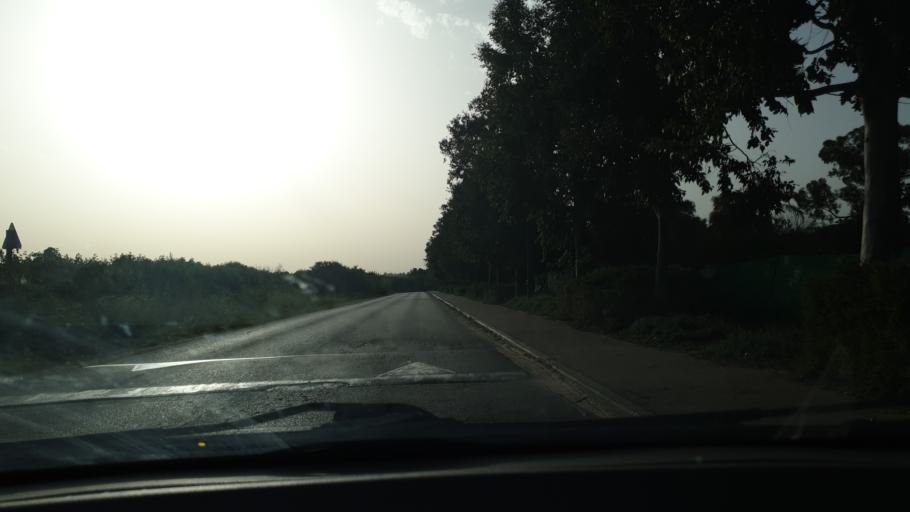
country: IL
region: Central District
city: Tel Mond
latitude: 32.2728
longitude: 34.9306
